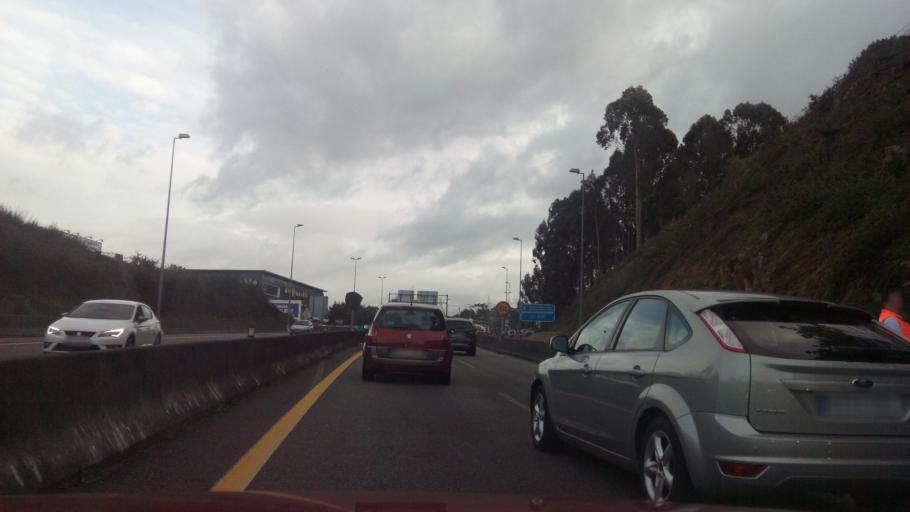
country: ES
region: Galicia
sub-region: Provincia de Pontevedra
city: Vigo
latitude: 42.2160
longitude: -8.6776
